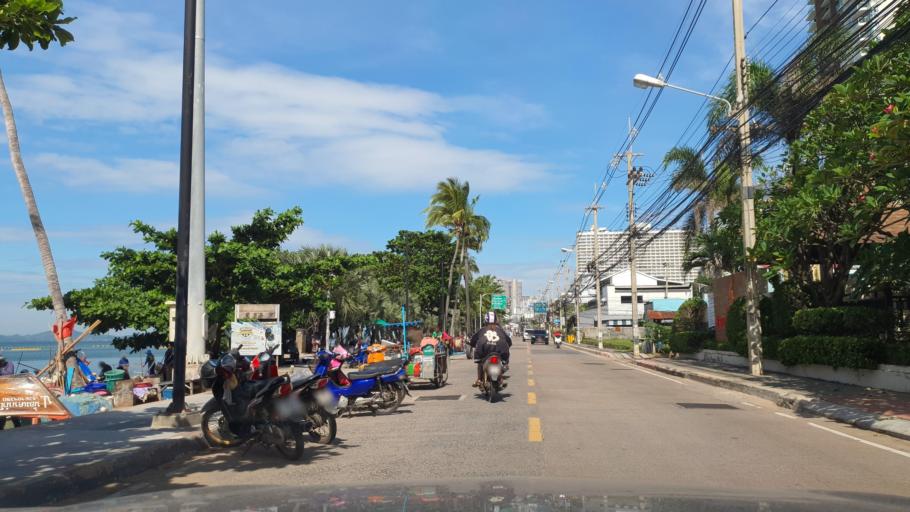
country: TH
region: Chon Buri
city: Phatthaya
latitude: 12.8733
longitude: 100.8880
